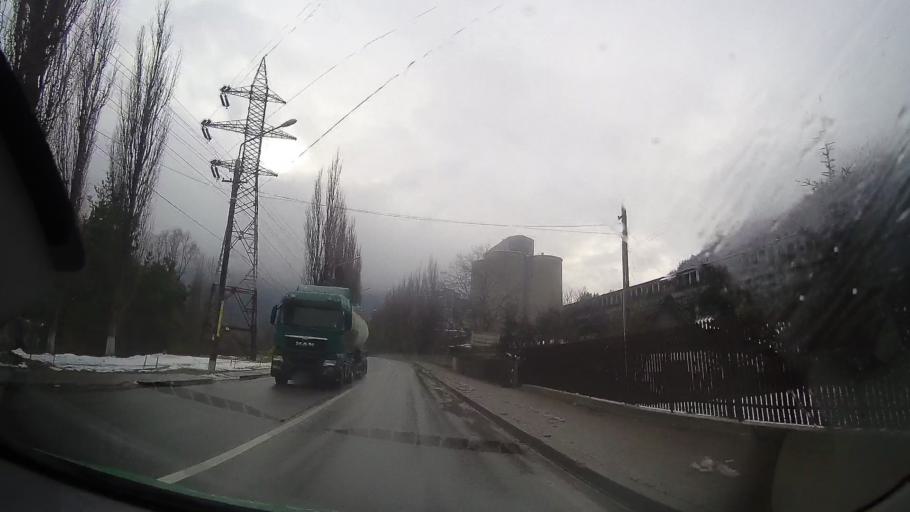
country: RO
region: Neamt
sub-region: Comuna Bicaz
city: Bicaz
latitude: 46.9063
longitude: 26.0768
